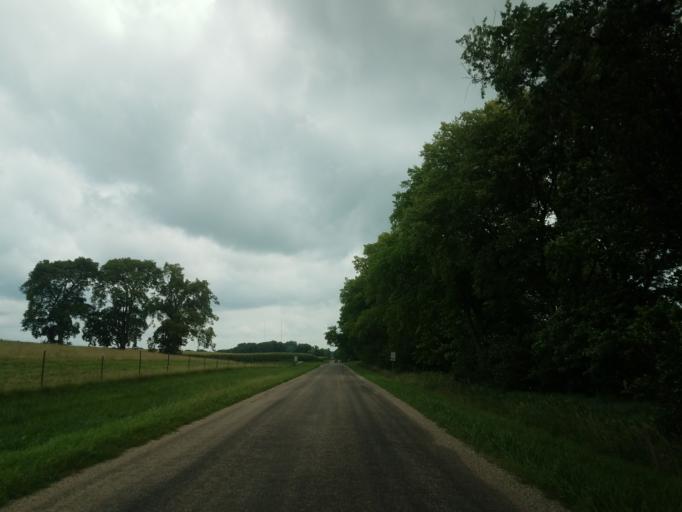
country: US
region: Illinois
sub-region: McLean County
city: Twin Grove
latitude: 40.4606
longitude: -89.0440
